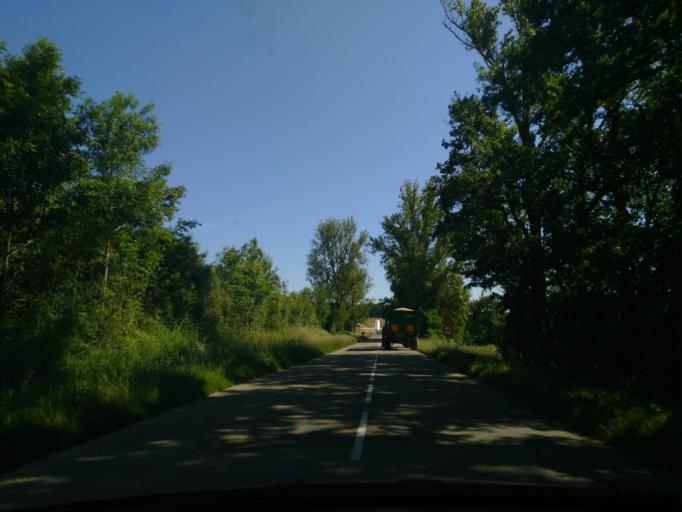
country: FR
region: Midi-Pyrenees
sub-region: Departement du Gers
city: Gimont
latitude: 43.6125
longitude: 0.8542
